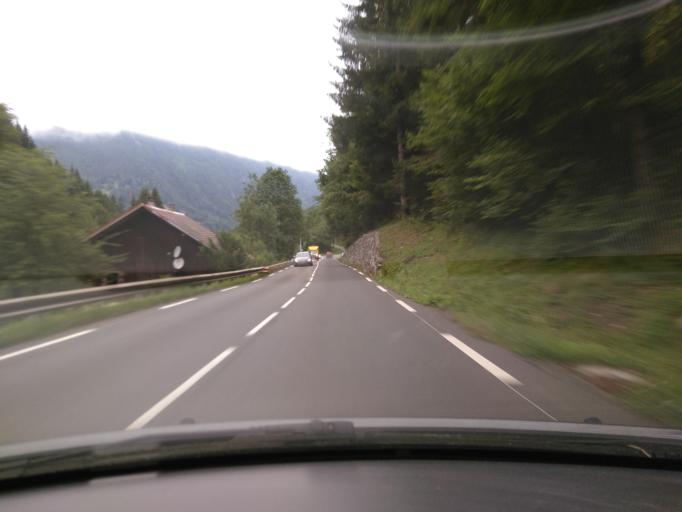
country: FR
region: Rhone-Alpes
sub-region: Departement de la Haute-Savoie
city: Saint-Jean-de-Sixt
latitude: 45.9453
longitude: 6.4020
